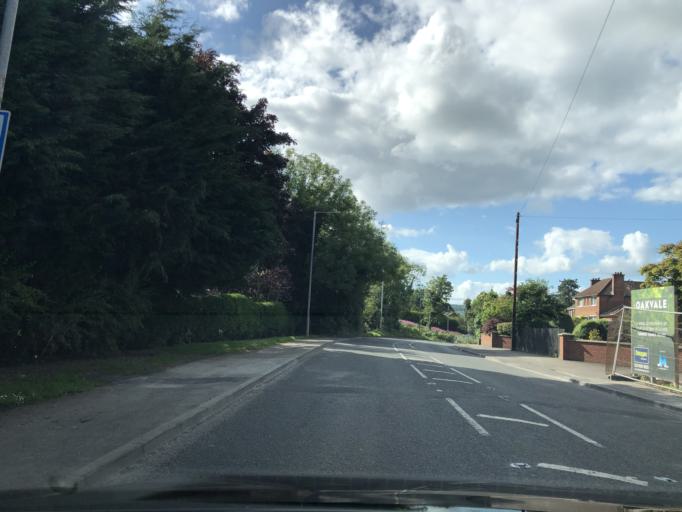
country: GB
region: Northern Ireland
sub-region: Castlereagh District
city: Dundonald
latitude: 54.5838
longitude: -5.7972
